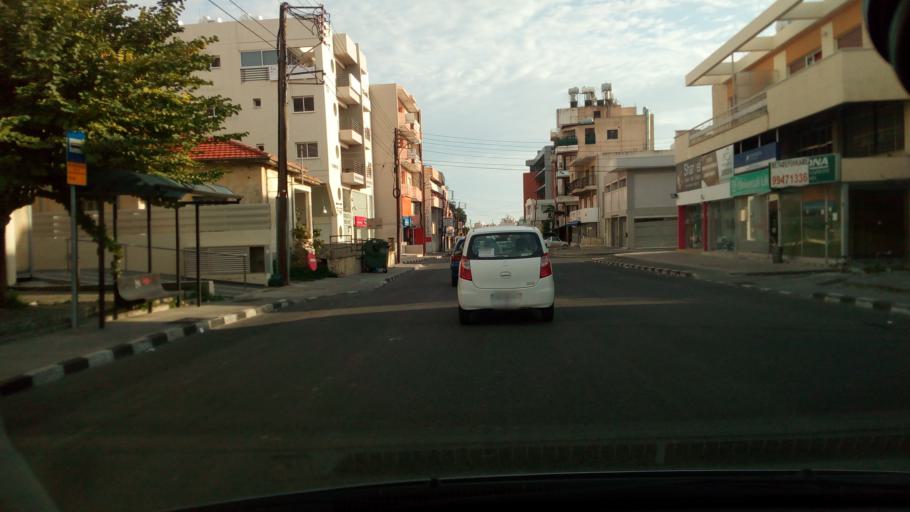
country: CY
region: Limassol
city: Limassol
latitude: 34.6808
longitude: 33.0396
